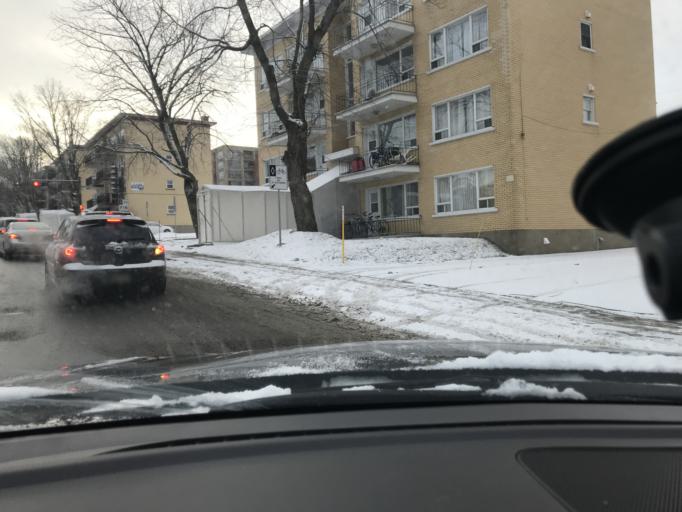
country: CA
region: Quebec
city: Quebec
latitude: 46.7916
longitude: -71.2739
